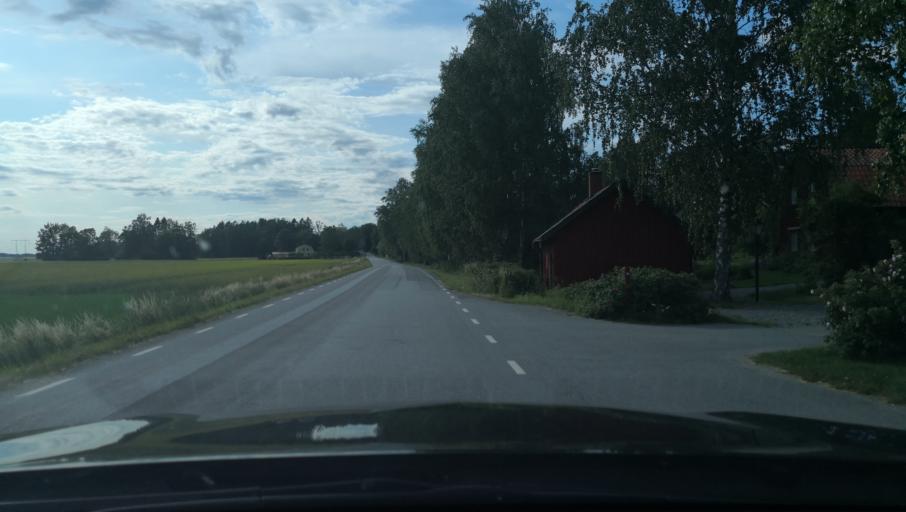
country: SE
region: Uppsala
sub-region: Enkopings Kommun
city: Orsundsbro
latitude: 59.6860
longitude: 17.3936
